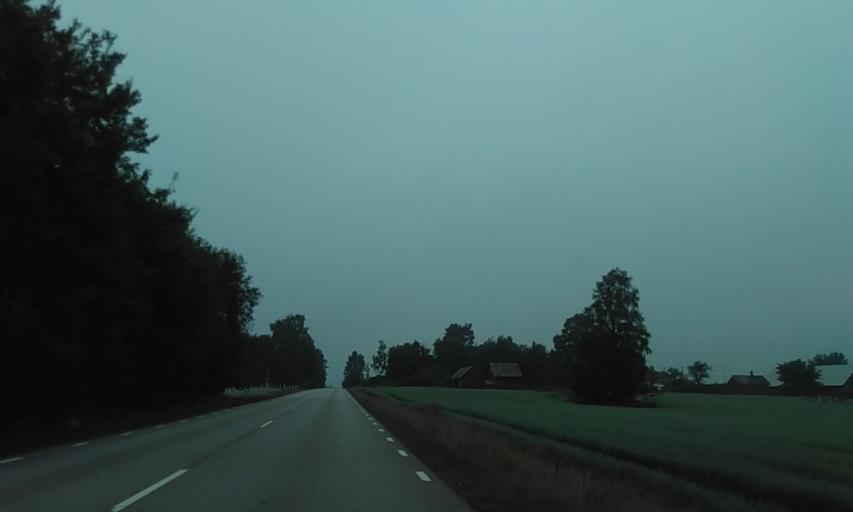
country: SE
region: Vaestra Goetaland
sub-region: Vargarda Kommun
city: Vargarda
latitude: 58.1496
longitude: 12.8566
